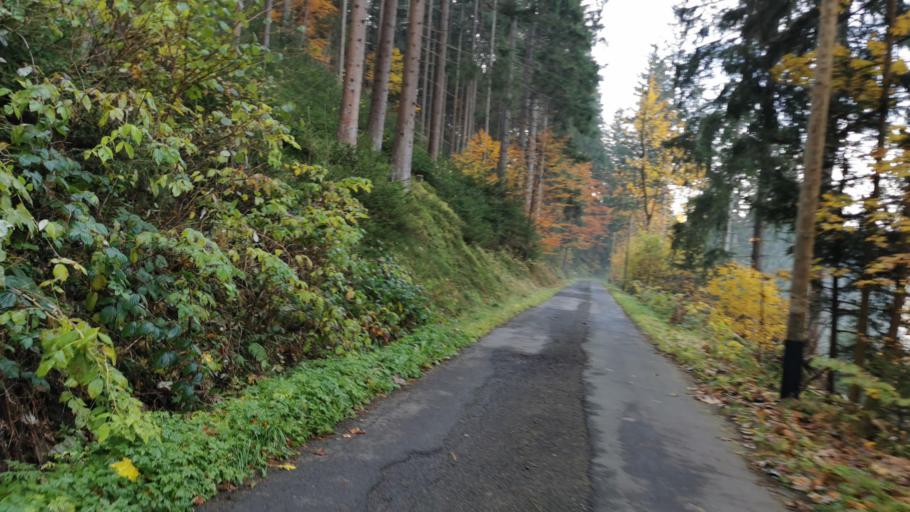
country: DE
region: Bavaria
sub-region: Upper Franconia
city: Nordhalben
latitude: 50.3743
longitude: 11.5238
